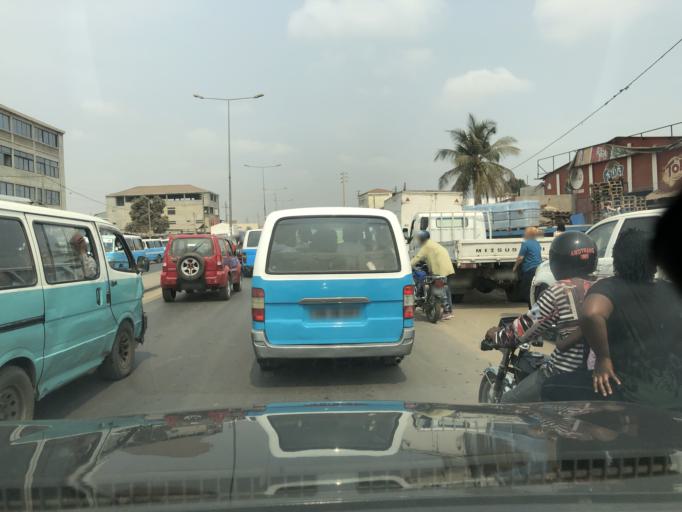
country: AO
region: Luanda
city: Luanda
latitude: -8.8009
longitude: 13.3115
